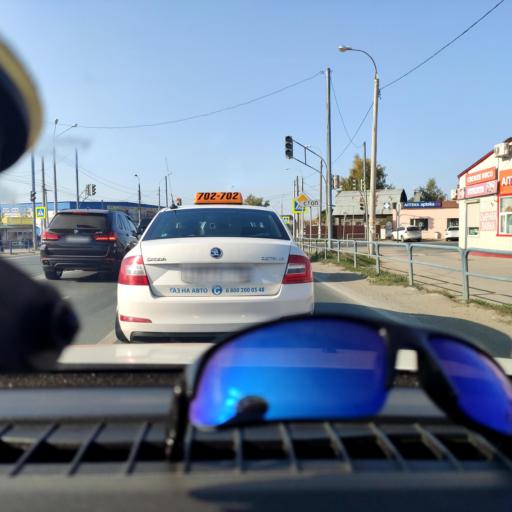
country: RU
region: Samara
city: Volzhskiy
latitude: 53.4260
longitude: 50.1220
